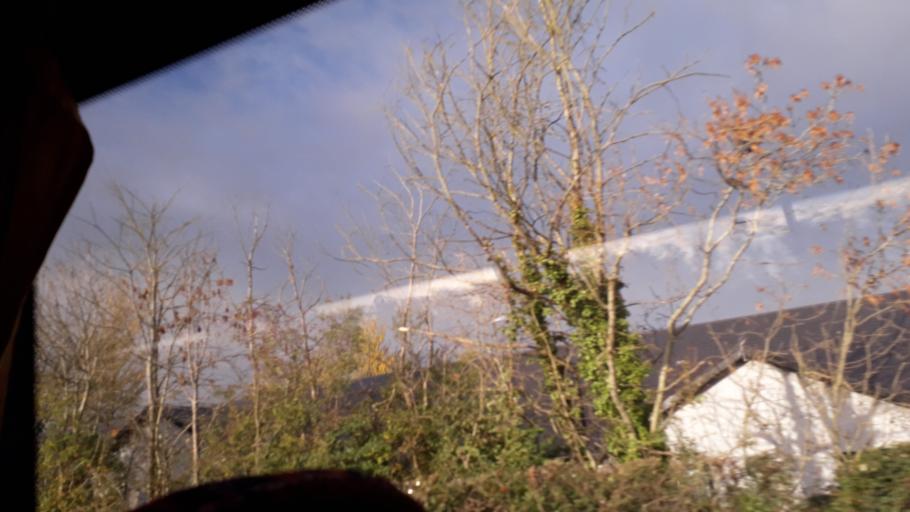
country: IE
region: Leinster
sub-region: Kildare
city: Maynooth
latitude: 53.3590
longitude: -6.5934
